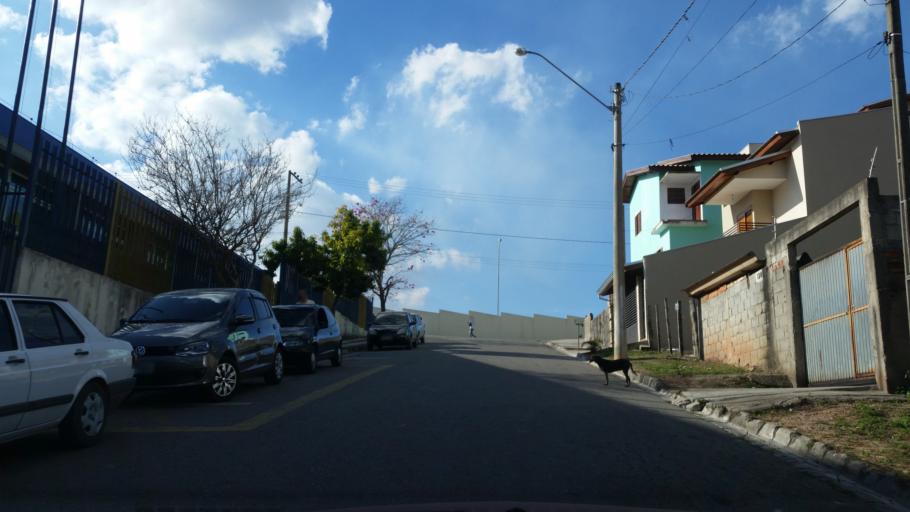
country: BR
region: Sao Paulo
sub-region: Mairinque
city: Mairinque
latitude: -23.5166
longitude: -47.2487
